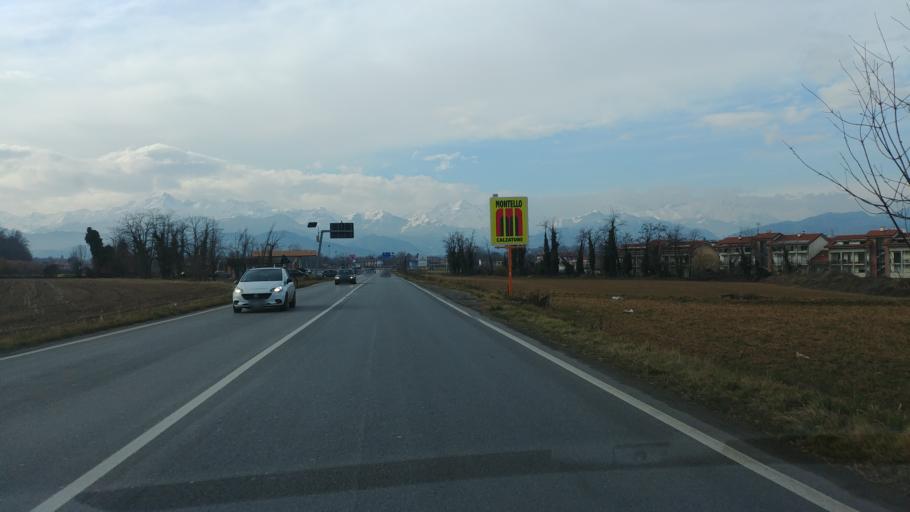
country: IT
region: Piedmont
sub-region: Provincia di Cuneo
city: Cuneo
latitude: 44.3886
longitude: 7.5711
